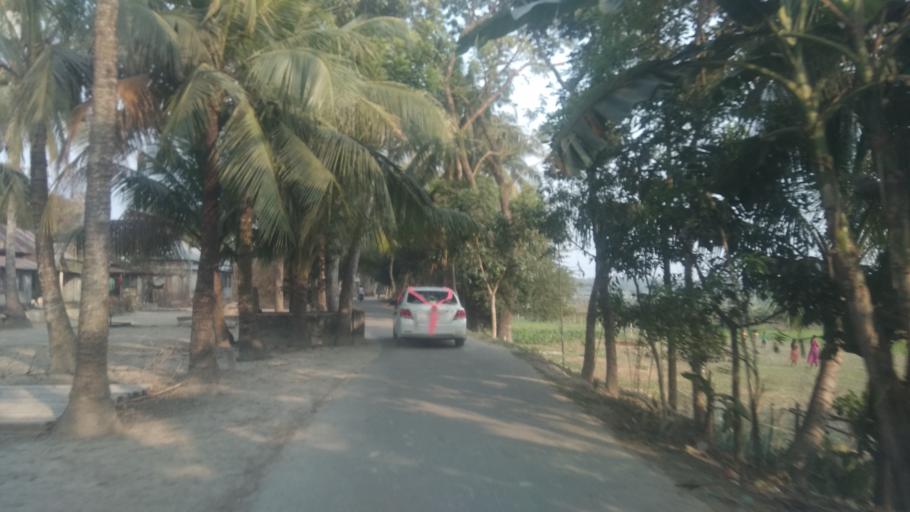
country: BD
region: Dhaka
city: Netrakona
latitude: 24.7756
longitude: 90.6045
